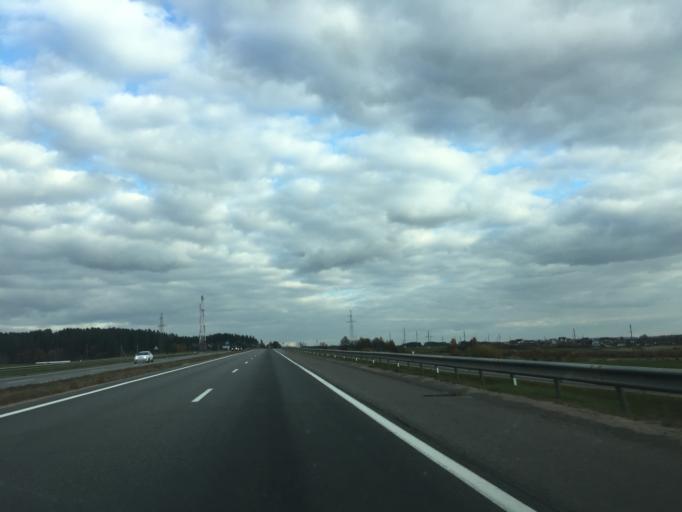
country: BY
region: Minsk
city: Rakaw
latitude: 53.9780
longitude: 27.0421
